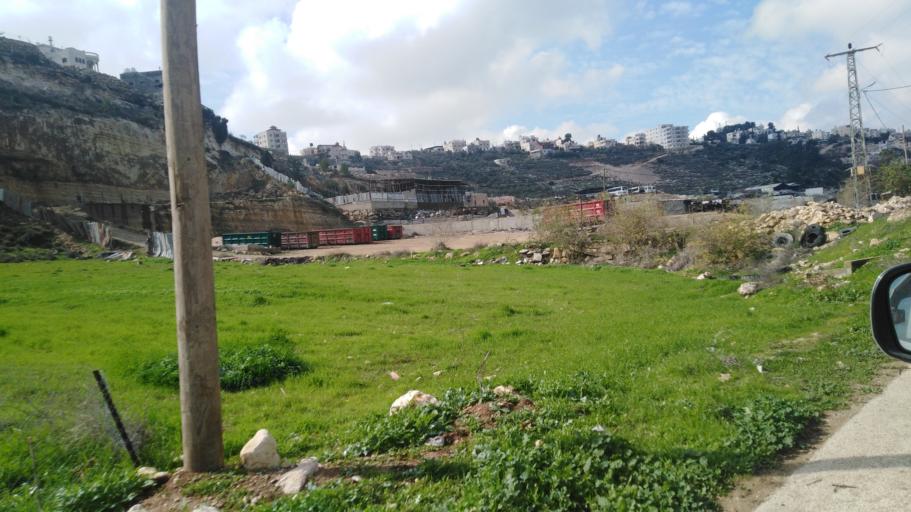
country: PS
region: West Bank
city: Idhna
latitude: 31.5561
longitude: 34.9903
